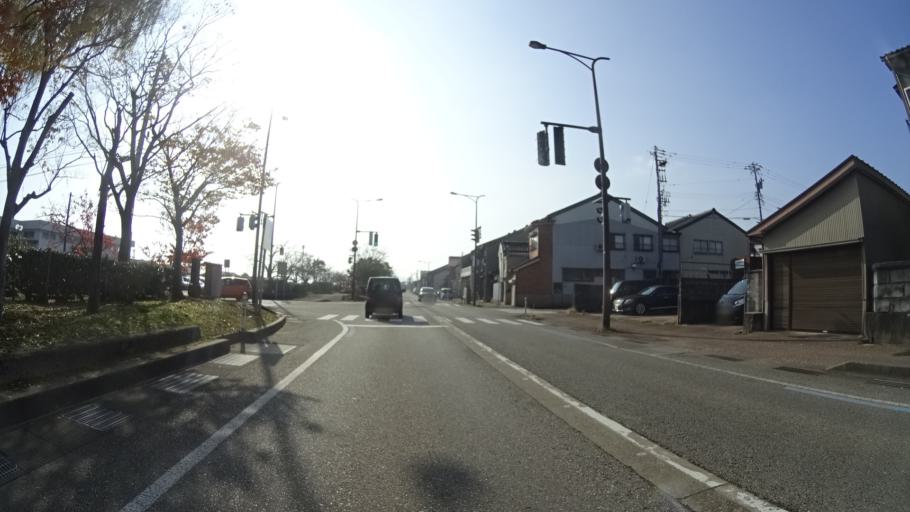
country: JP
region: Toyama
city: Himi
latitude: 36.8577
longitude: 136.9892
